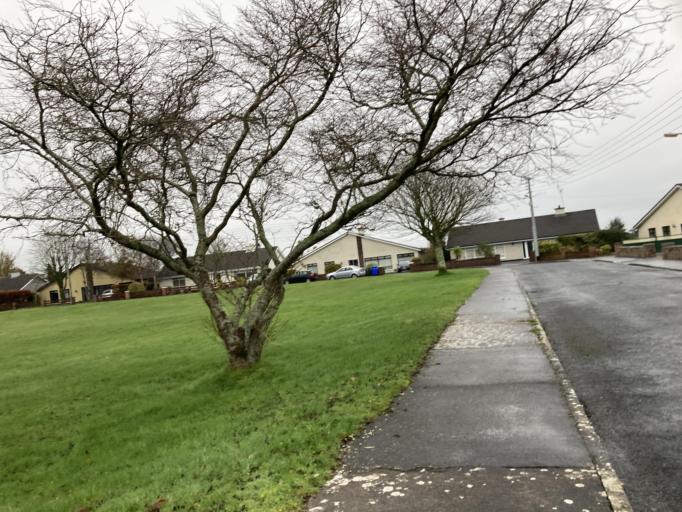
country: IE
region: Connaught
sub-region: County Galway
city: Oranmore
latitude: 53.2616
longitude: -8.9292
